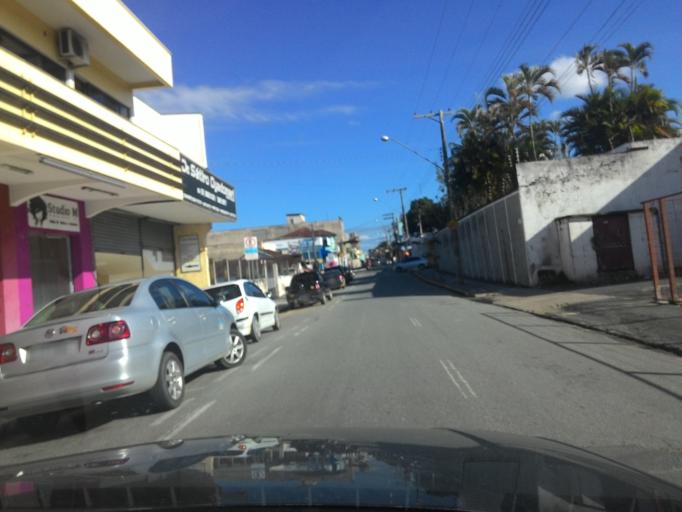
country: BR
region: Sao Paulo
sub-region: Registro
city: Registro
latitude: -24.4936
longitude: -47.8424
